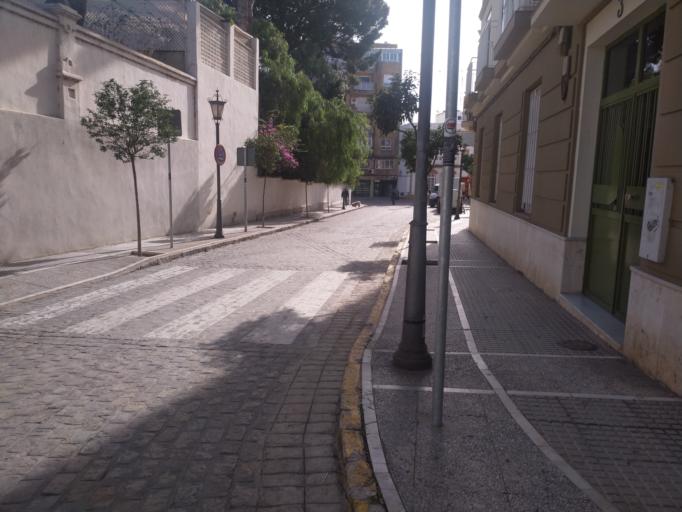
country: ES
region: Andalusia
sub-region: Provincia de Cadiz
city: San Fernando
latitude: 36.4673
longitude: -6.1943
